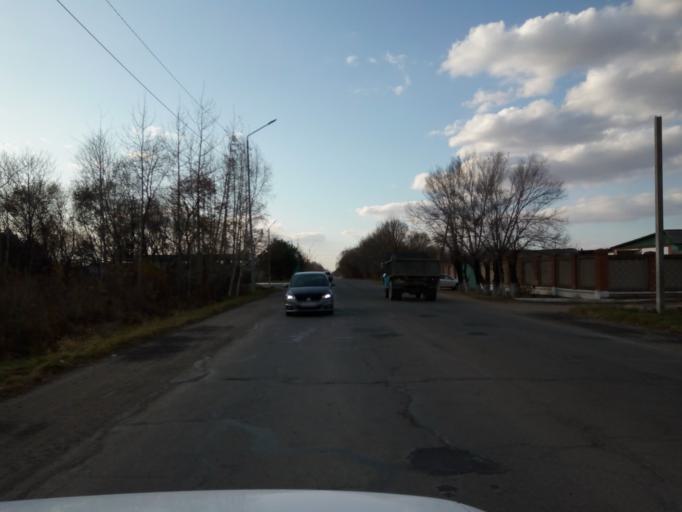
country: RU
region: Primorskiy
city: Dal'nerechensk
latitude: 45.9174
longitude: 133.7633
